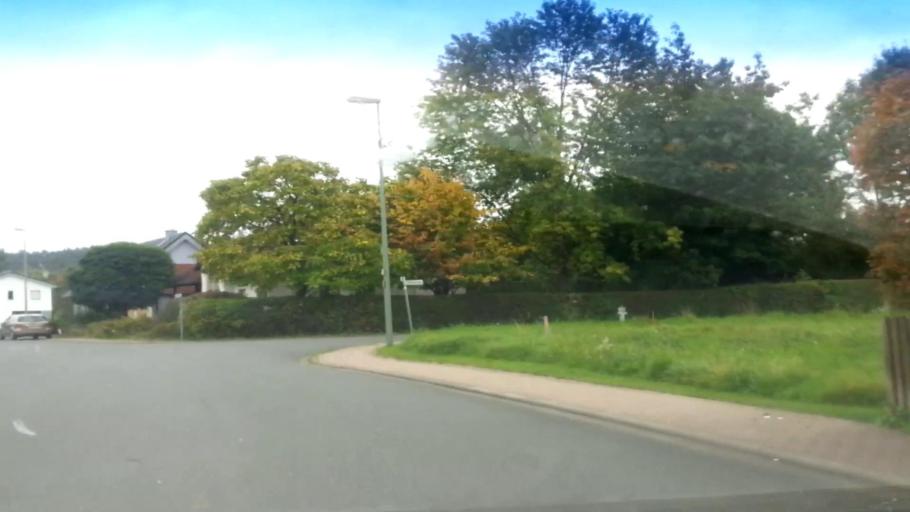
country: DE
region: Bavaria
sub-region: Upper Franconia
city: Zapfendorf
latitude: 50.0119
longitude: 10.9285
